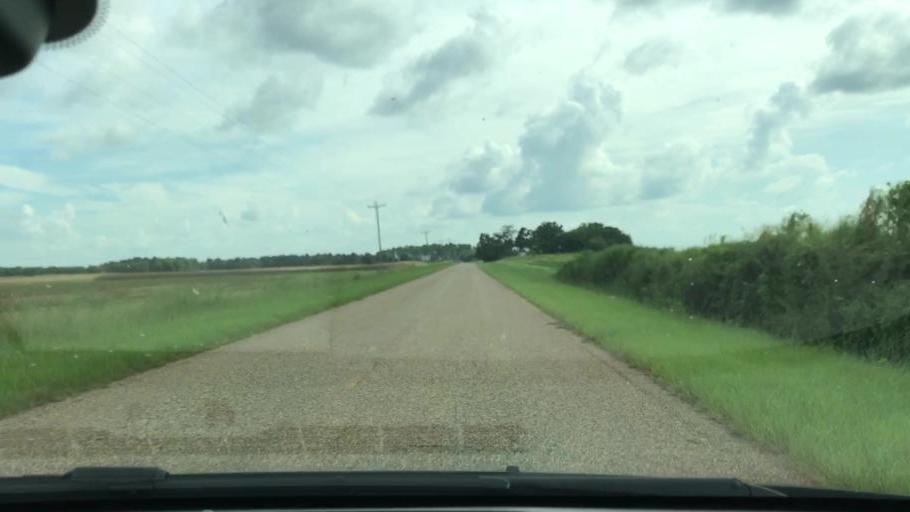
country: US
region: Georgia
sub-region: Clay County
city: Fort Gaines
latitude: 31.5258
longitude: -84.9544
